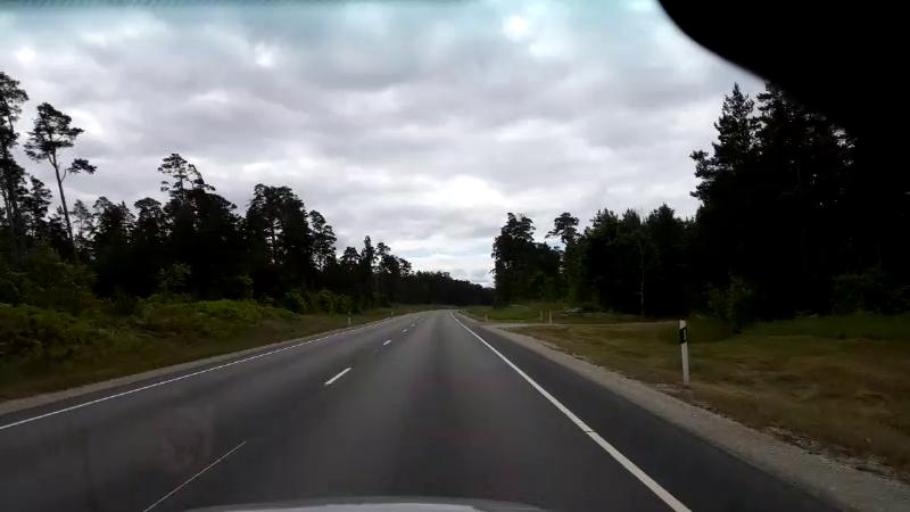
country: EE
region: Paernumaa
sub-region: Paernu linn
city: Parnu
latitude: 58.1888
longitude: 24.4914
